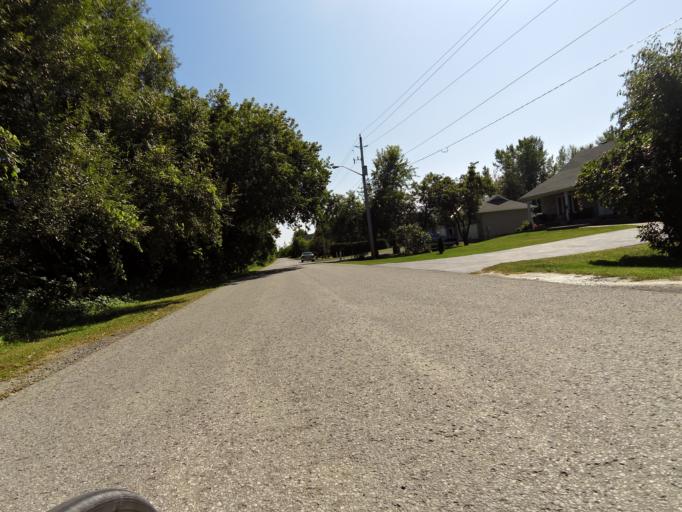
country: CA
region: Ontario
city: Bells Corners
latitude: 45.3499
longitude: -75.9034
